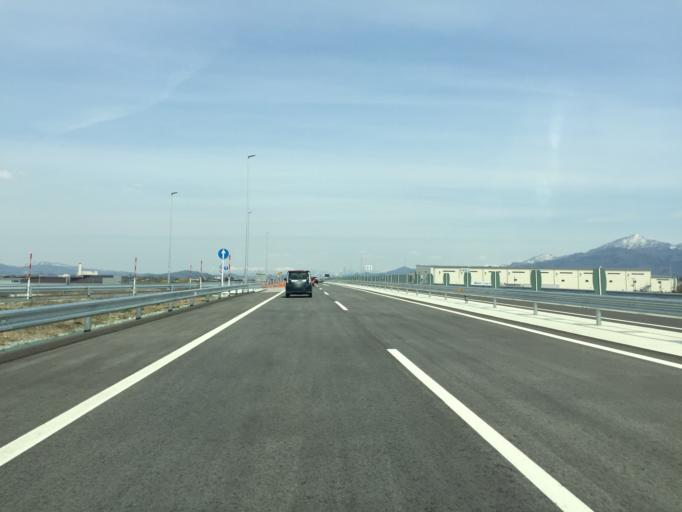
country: JP
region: Yamagata
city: Tendo
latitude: 38.4080
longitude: 140.3465
